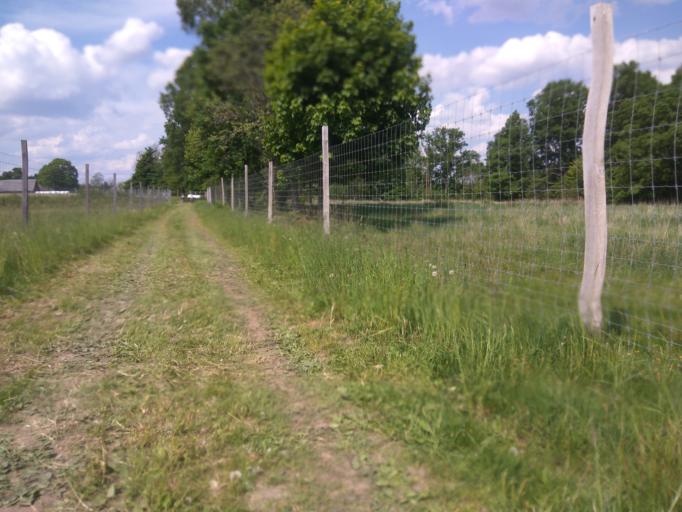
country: LV
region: Kuldigas Rajons
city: Kuldiga
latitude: 56.8899
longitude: 21.9299
